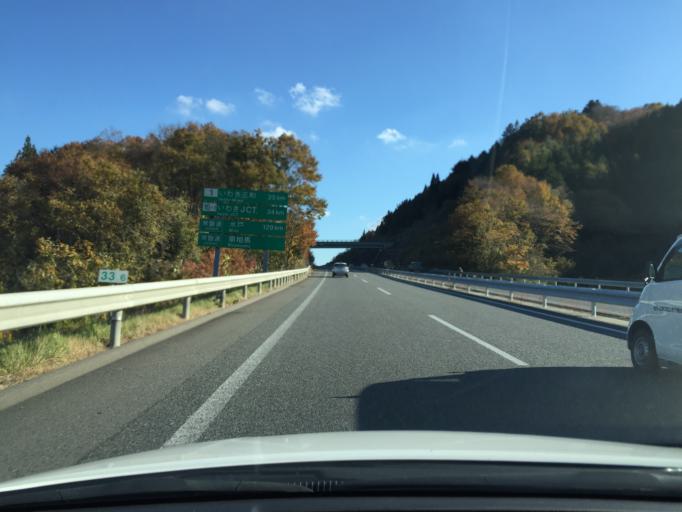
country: JP
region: Fukushima
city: Funehikimachi-funehiki
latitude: 37.2785
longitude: 140.6210
